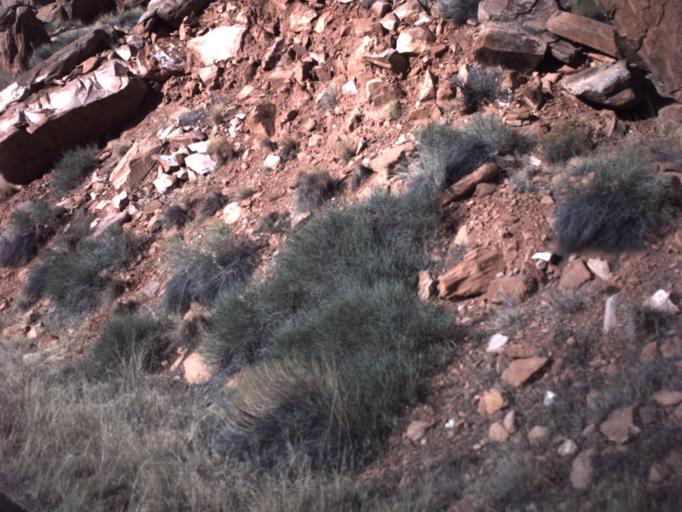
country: US
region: Utah
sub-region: Grand County
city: Moab
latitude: 38.7792
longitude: -109.3313
